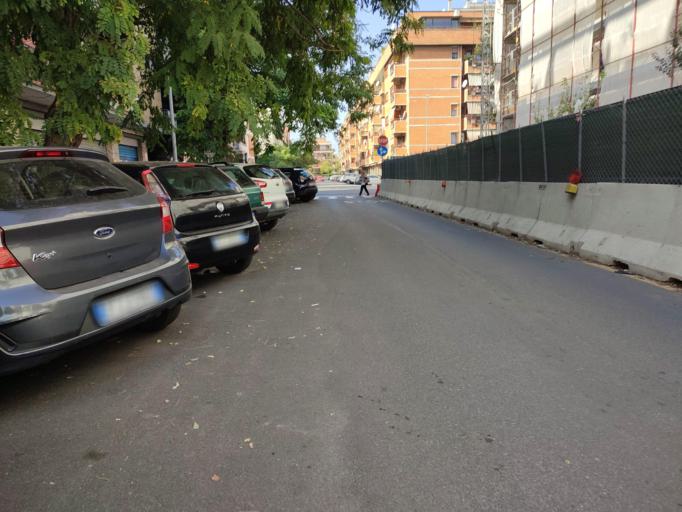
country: IT
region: Latium
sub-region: Citta metropolitana di Roma Capitale
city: Lido di Ostia
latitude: 41.7335
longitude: 12.2909
